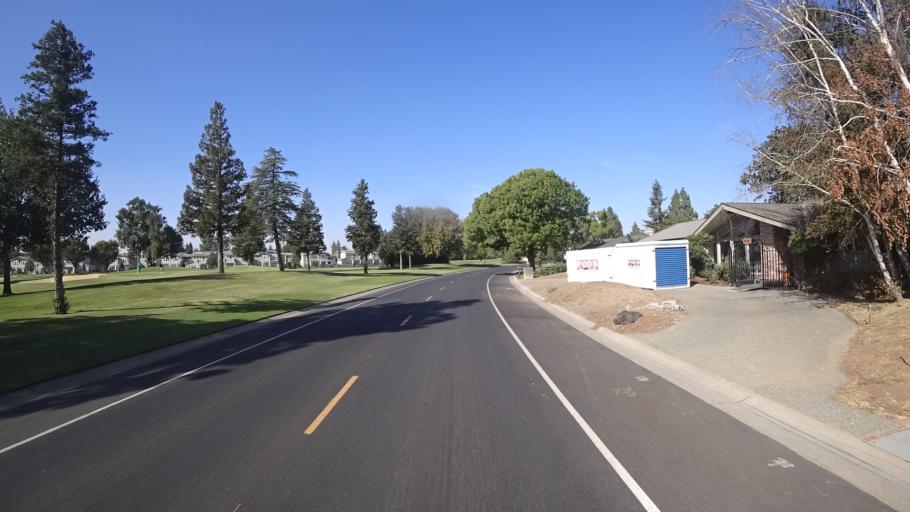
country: US
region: California
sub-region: Yolo County
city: Davis
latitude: 38.5449
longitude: -121.6918
